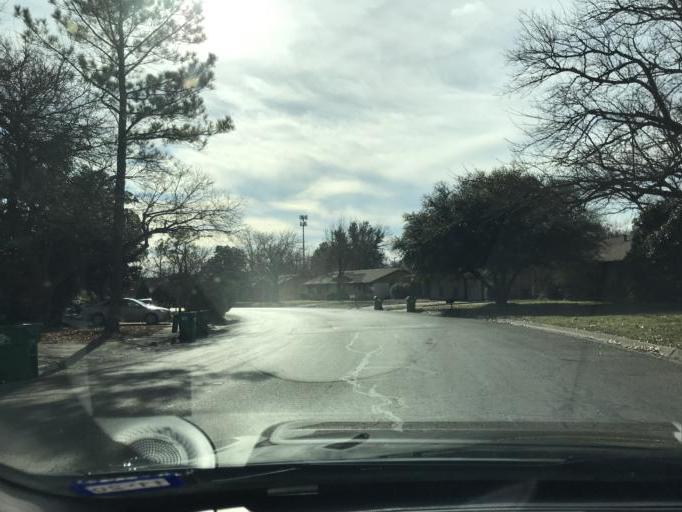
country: US
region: Texas
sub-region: Denton County
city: Denton
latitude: 33.2329
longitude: -97.1491
